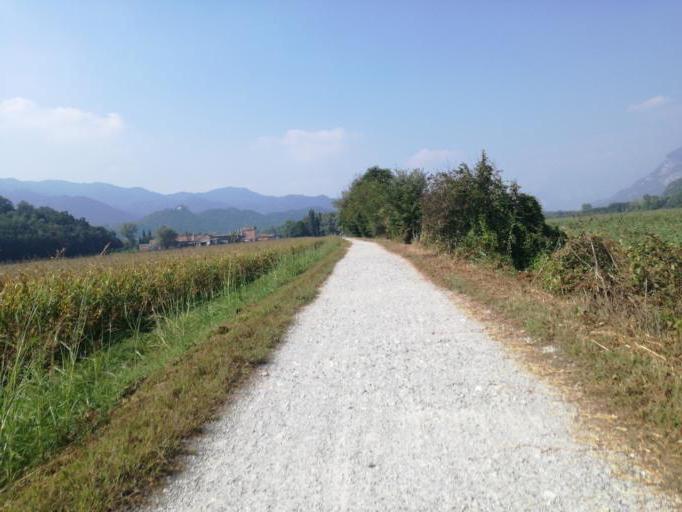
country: IT
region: Lombardy
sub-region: Provincia di Lecco
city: Brivio
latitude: 45.7504
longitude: 9.4503
